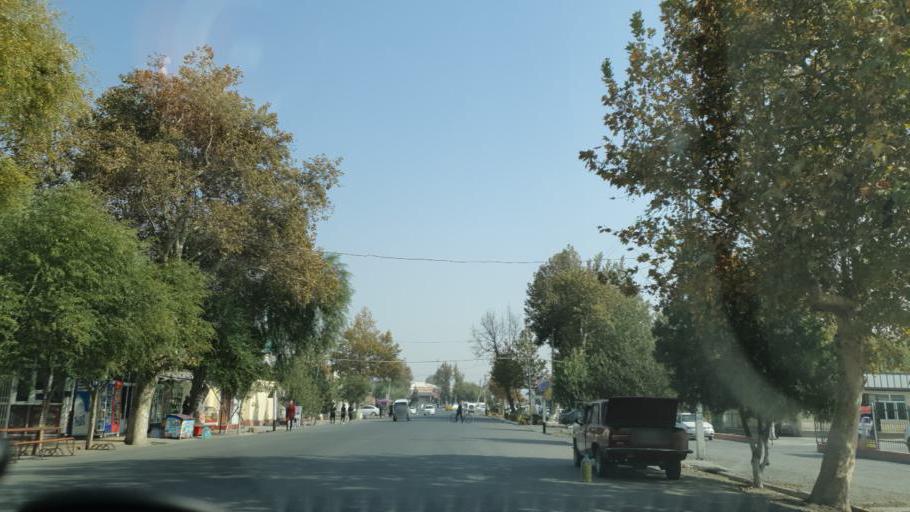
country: UZ
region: Fergana
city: Beshariq
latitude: 40.4361
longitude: 70.6004
